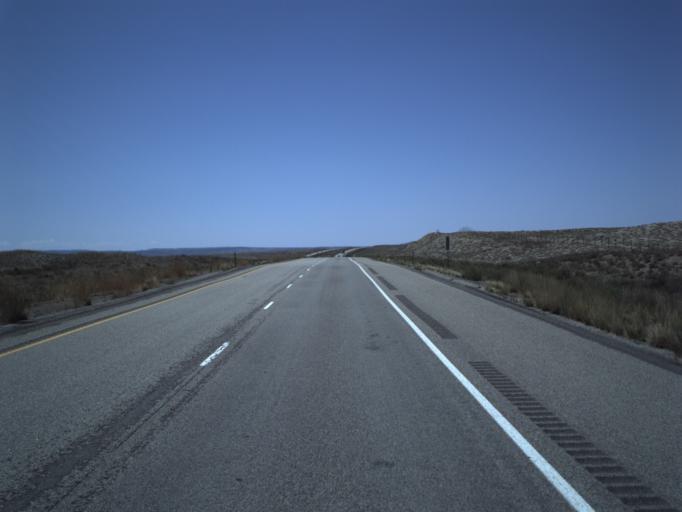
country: US
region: Utah
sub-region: Grand County
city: Moab
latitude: 39.0219
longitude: -109.2981
